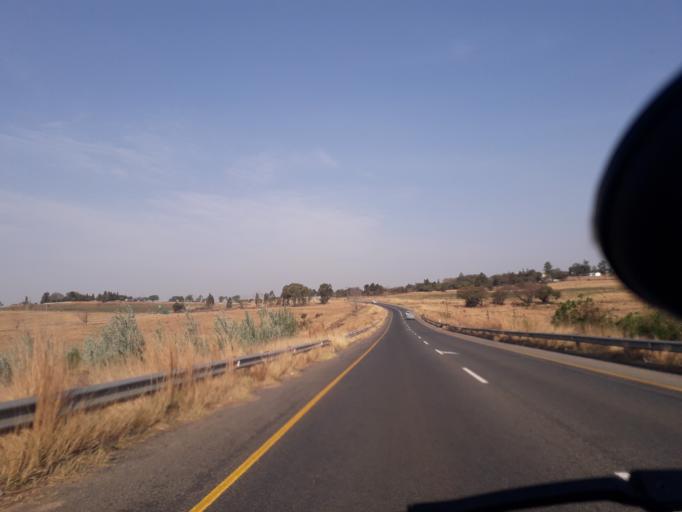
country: ZA
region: Gauteng
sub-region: West Rand District Municipality
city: Muldersdriseloop
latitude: -25.9682
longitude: 27.9053
